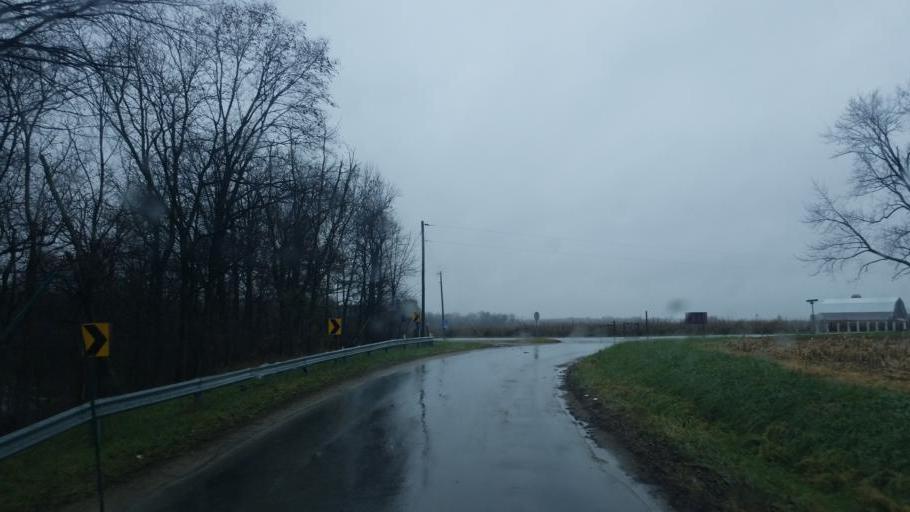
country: US
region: Indiana
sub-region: Adams County
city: Geneva
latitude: 40.6160
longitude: -84.9352
